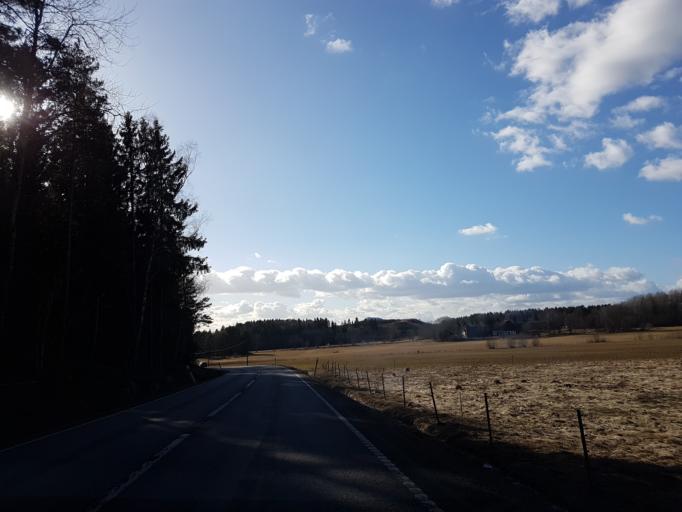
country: SE
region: Stockholm
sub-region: Norrtalje Kommun
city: Rimbo
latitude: 59.7371
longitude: 18.4567
